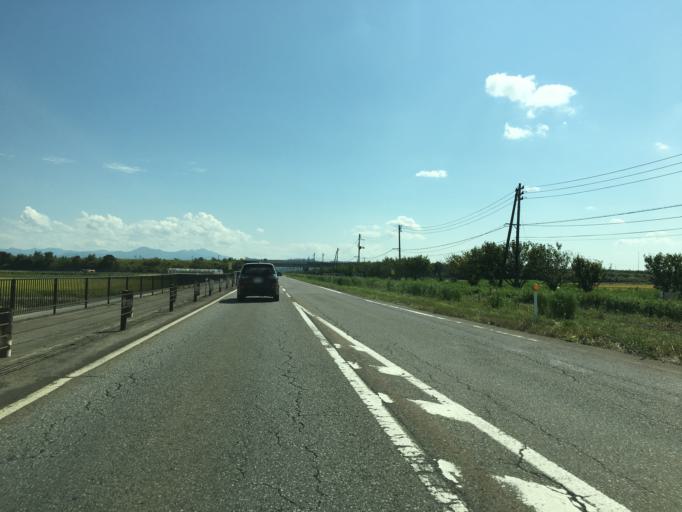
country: JP
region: Niigata
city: Niitsu-honcho
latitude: 37.8243
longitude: 139.0984
